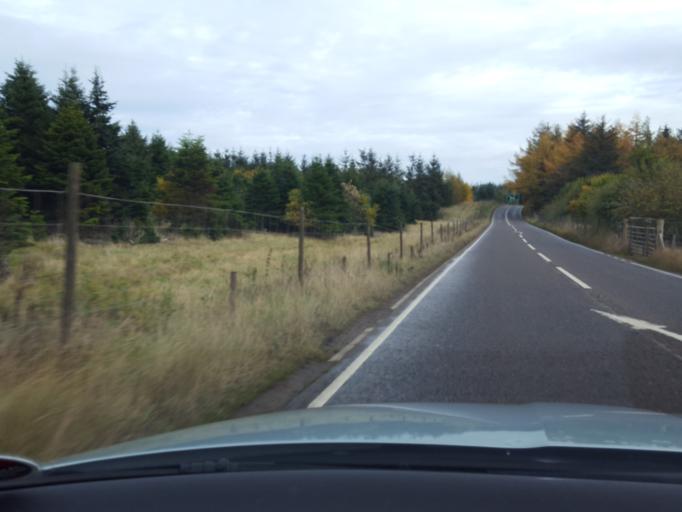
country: GB
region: Scotland
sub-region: South Lanarkshire
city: Biggar
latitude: 55.6829
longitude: -3.4621
